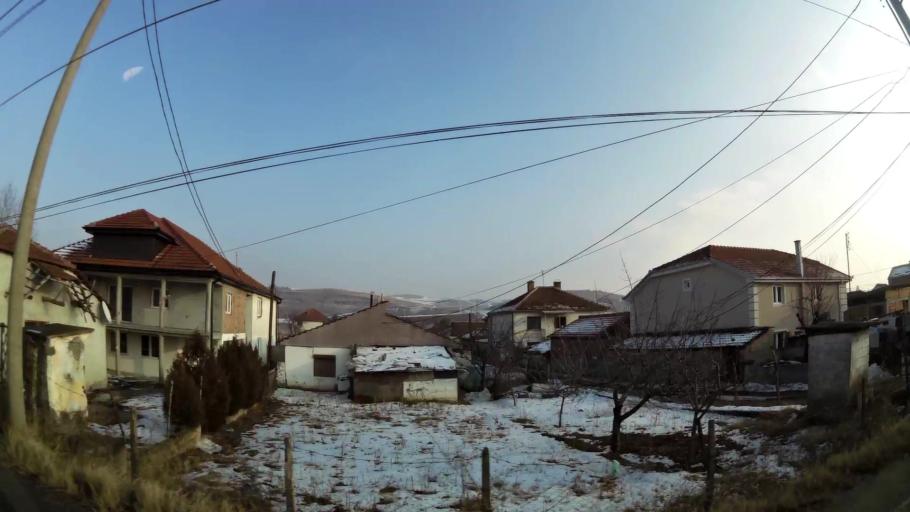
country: MK
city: Miladinovci
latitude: 41.9910
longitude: 21.6539
